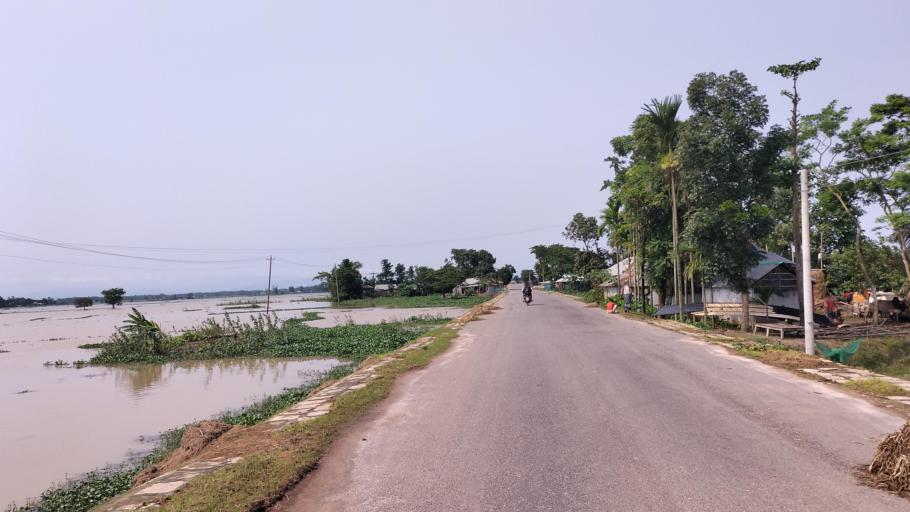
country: BD
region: Dhaka
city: Netrakona
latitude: 25.0145
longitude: 90.8543
